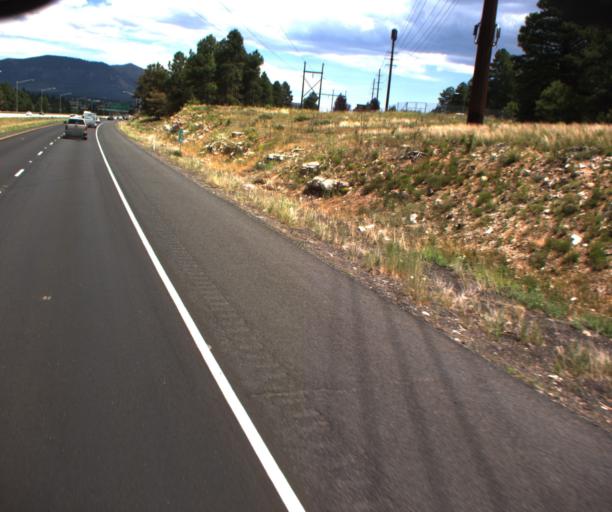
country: US
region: Arizona
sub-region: Coconino County
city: Flagstaff
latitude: 35.1611
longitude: -111.6755
